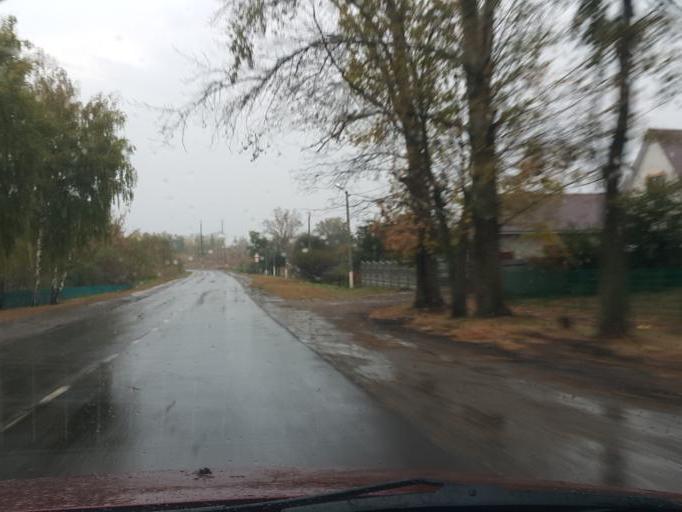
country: RU
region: Tambov
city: Znamenka
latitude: 52.4077
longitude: 41.4573
